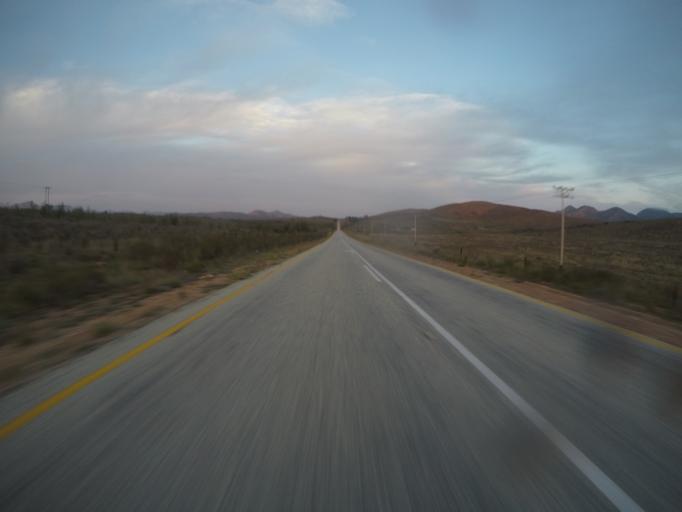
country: ZA
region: Western Cape
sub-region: Eden District Municipality
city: Plettenberg Bay
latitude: -33.7385
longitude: 23.4234
